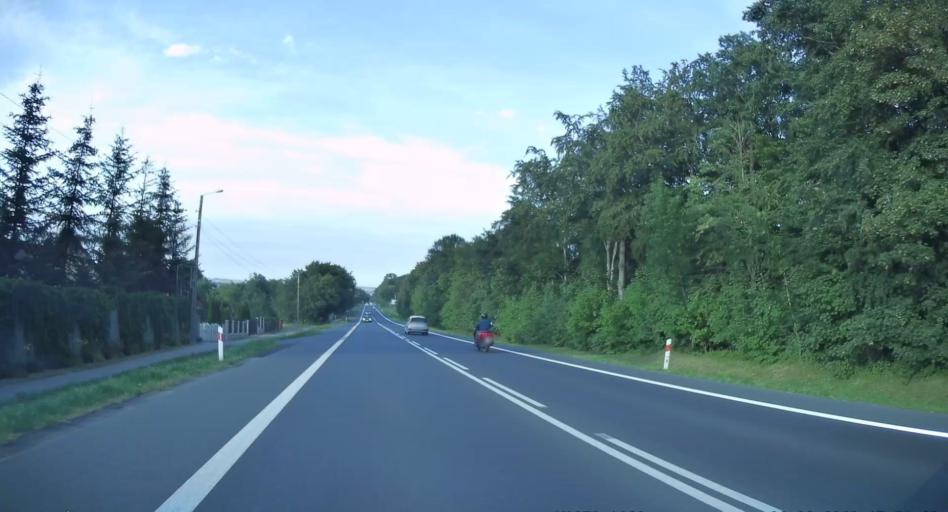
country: PL
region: Lesser Poland Voivodeship
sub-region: Powiat krakowski
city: Slomniki
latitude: 50.2154
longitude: 20.0276
